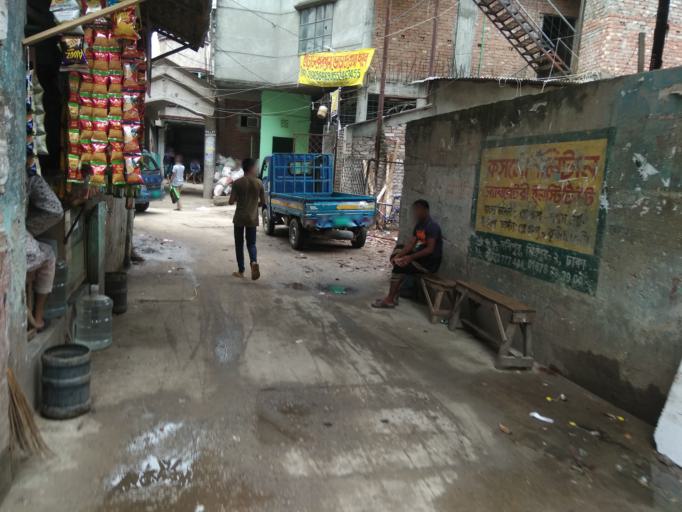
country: BD
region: Dhaka
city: Azimpur
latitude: 23.8013
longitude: 90.3706
